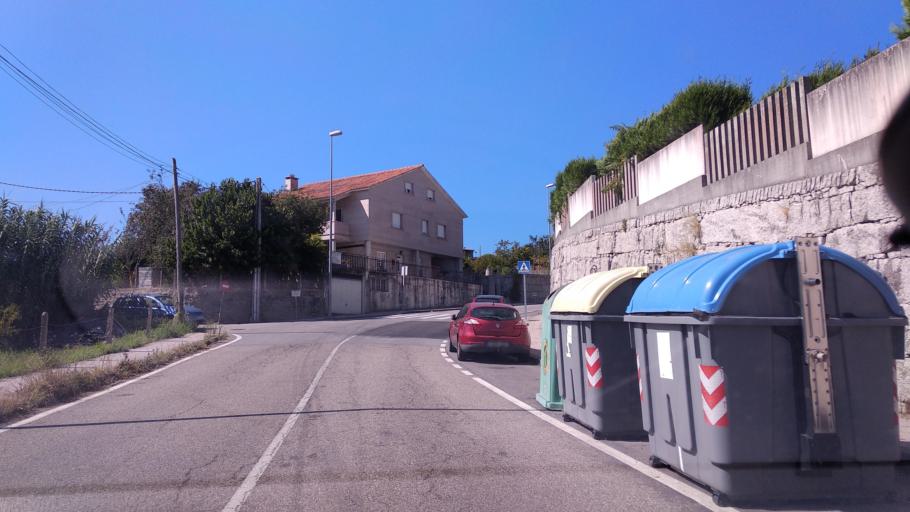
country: ES
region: Galicia
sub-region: Provincia de Pontevedra
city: Moana
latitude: 42.2764
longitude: -8.7683
